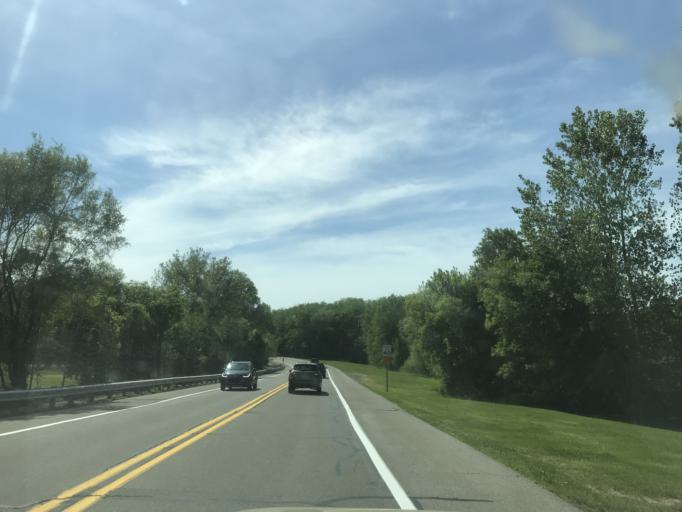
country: US
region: Michigan
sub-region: Wayne County
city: Dearborn Heights
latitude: 42.3521
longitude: -83.3007
